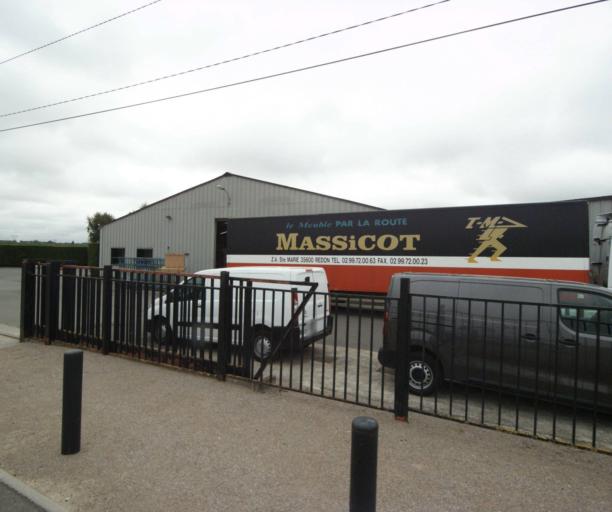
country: FR
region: Nord-Pas-de-Calais
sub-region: Departement du Nord
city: Lesquin
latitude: 50.5945
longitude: 3.1120
